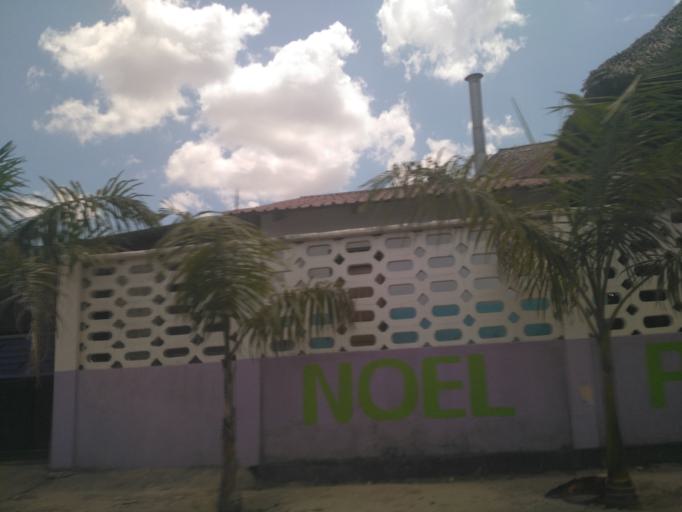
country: TZ
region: Dar es Salaam
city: Dar es Salaam
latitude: -6.8486
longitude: 39.2648
